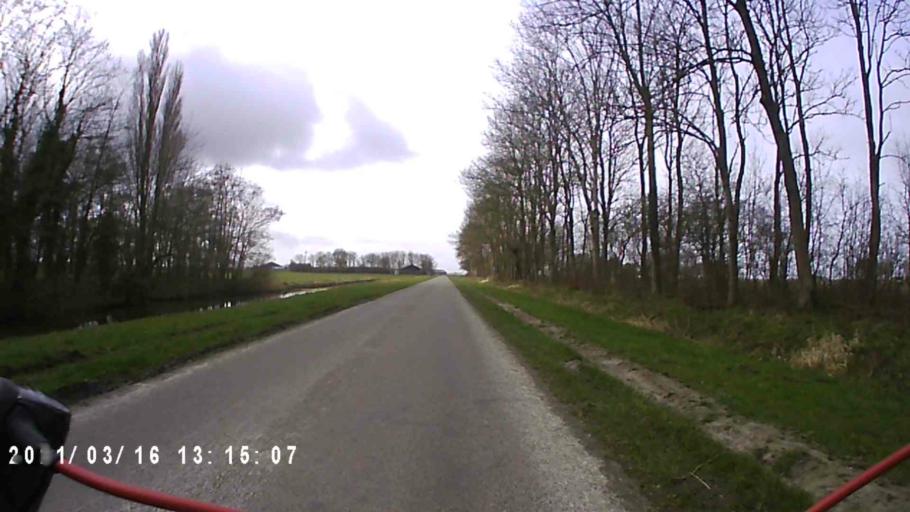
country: NL
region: Friesland
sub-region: Gemeente Het Bildt
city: Minnertsga
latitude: 53.2389
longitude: 5.5983
